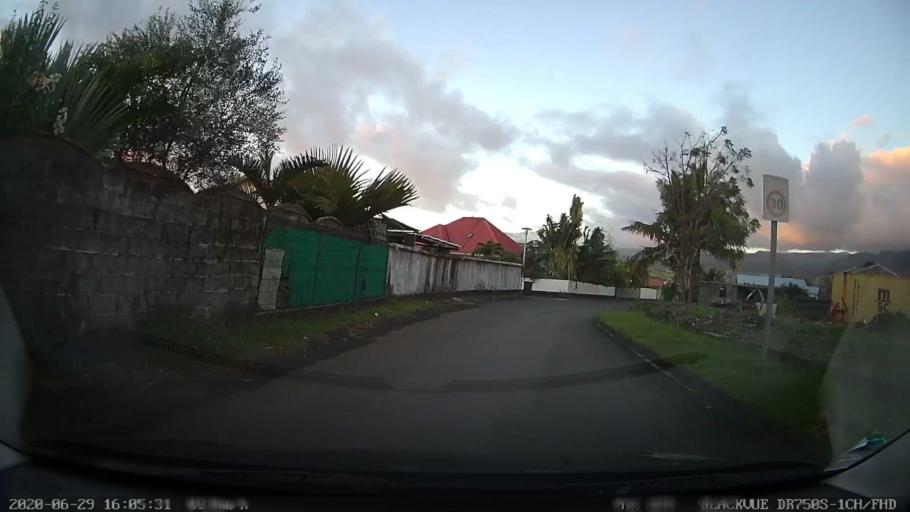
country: RE
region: Reunion
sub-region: Reunion
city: Bras-Panon
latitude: -20.9921
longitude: 55.6821
